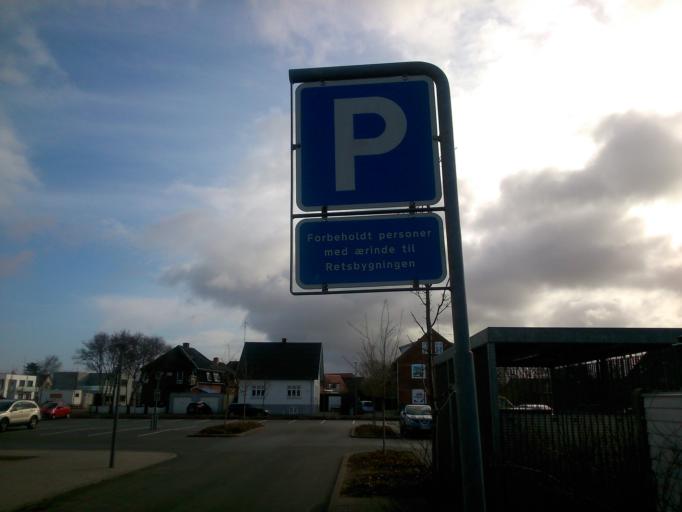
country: DK
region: Central Jutland
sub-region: Holstebro Kommune
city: Holstebro
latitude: 56.3680
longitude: 8.6221
